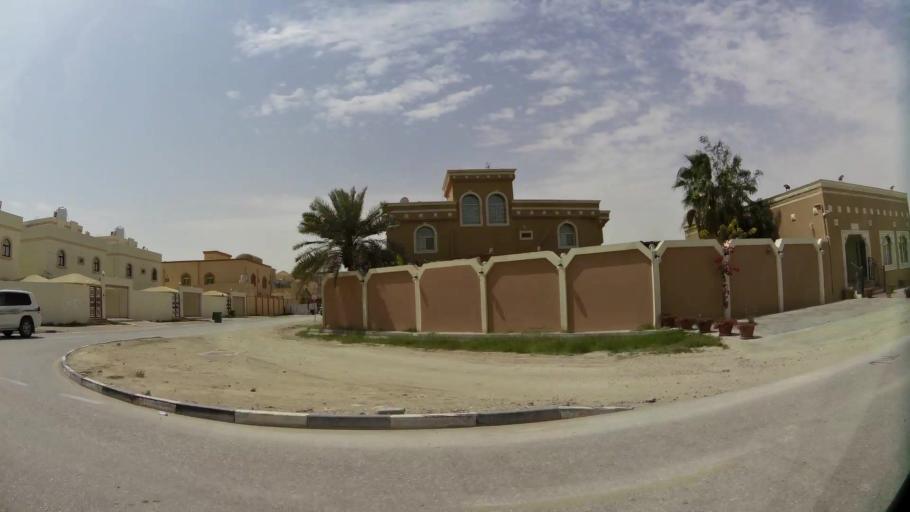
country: QA
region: Baladiyat ar Rayyan
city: Ar Rayyan
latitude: 25.3517
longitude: 51.4764
